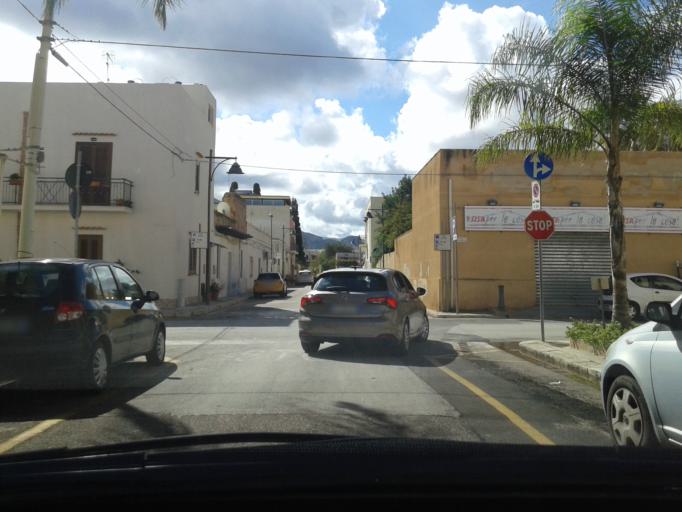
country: IT
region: Sicily
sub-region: Trapani
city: San Vito Lo Capo
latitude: 38.1726
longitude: 12.7345
